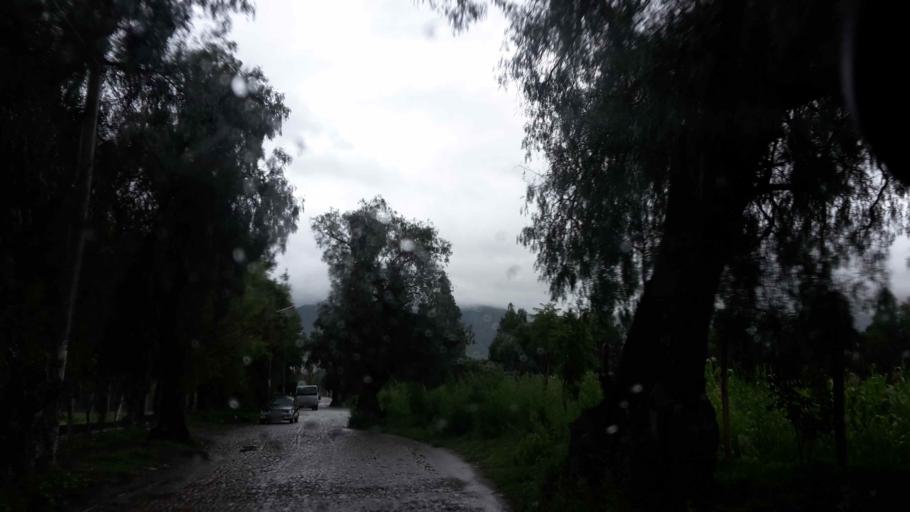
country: BO
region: Cochabamba
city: Cochabamba
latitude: -17.3646
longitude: -66.2134
